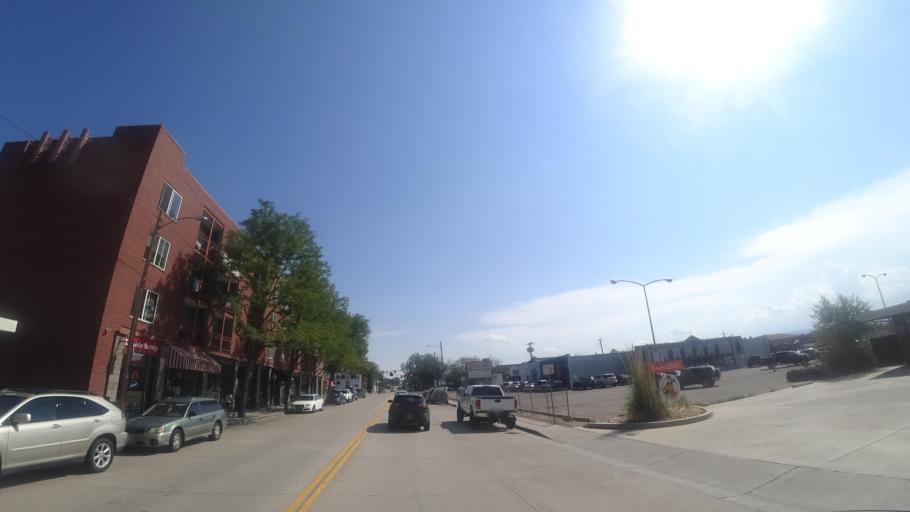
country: US
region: Colorado
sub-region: Arapahoe County
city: Littleton
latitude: 39.6149
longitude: -105.0162
